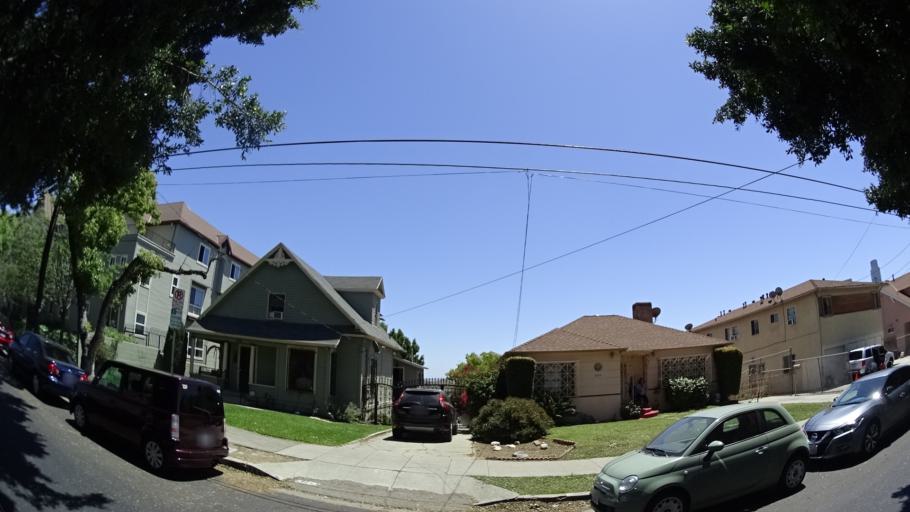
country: US
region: California
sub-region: Los Angeles County
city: Echo Park
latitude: 34.0656
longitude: -118.2554
